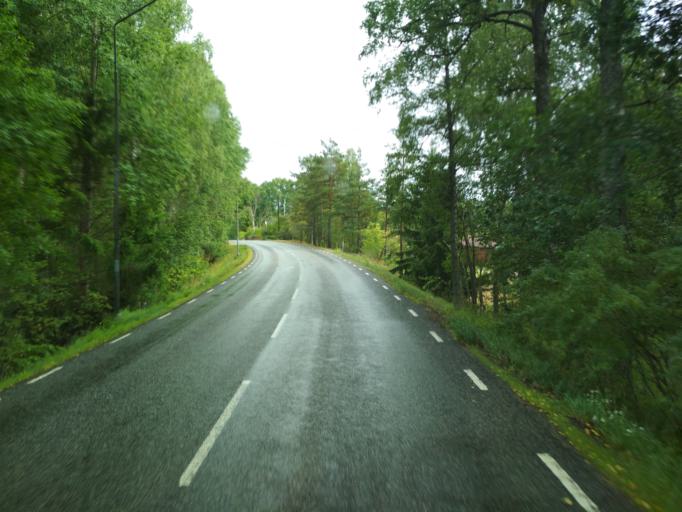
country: SE
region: Vaestmanland
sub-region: Surahammars Kommun
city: Ramnas
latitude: 59.7896
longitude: 16.1802
